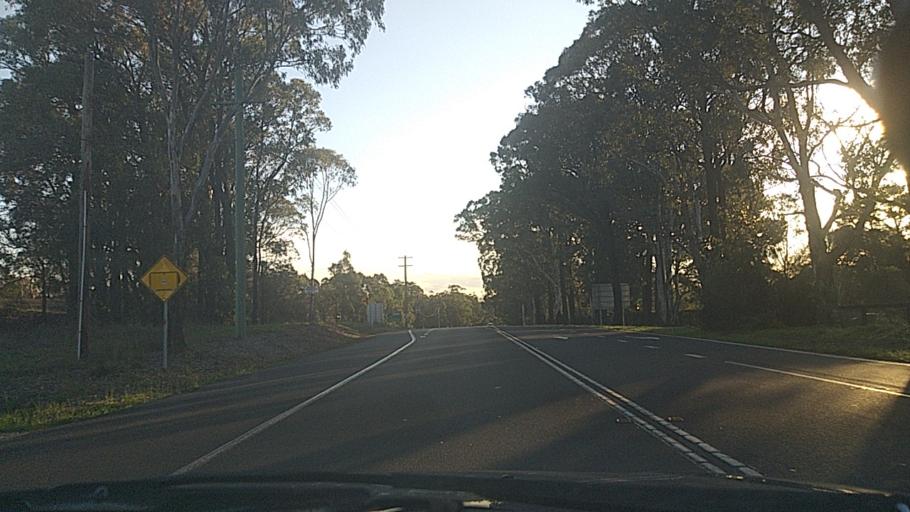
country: AU
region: New South Wales
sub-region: Wollondilly
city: Douglas Park
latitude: -34.2373
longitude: 150.7290
